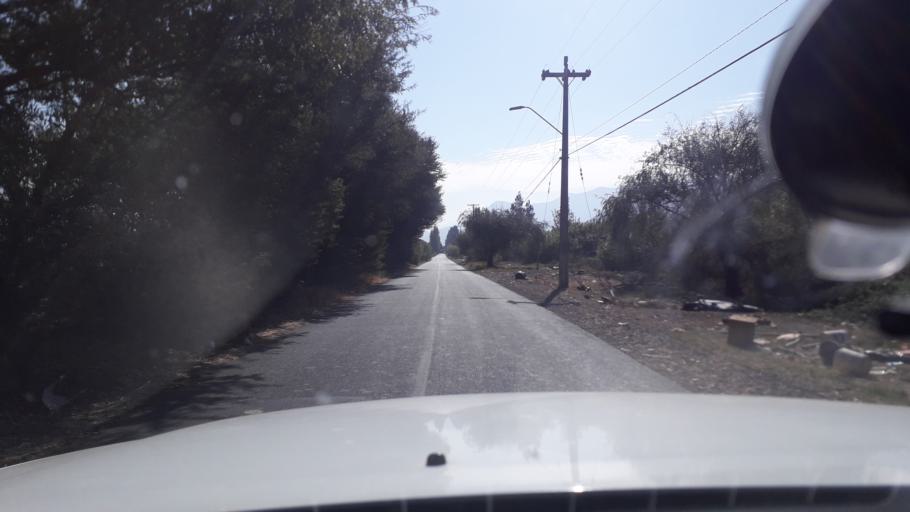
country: CL
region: Valparaiso
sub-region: Provincia de San Felipe
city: Llaillay
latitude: -32.8562
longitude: -70.9383
